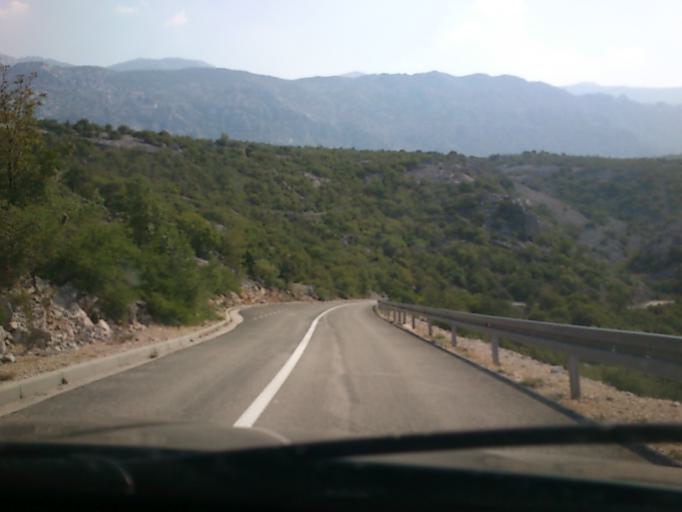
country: HR
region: Primorsko-Goranska
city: Banjol
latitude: 44.7091
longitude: 14.9009
